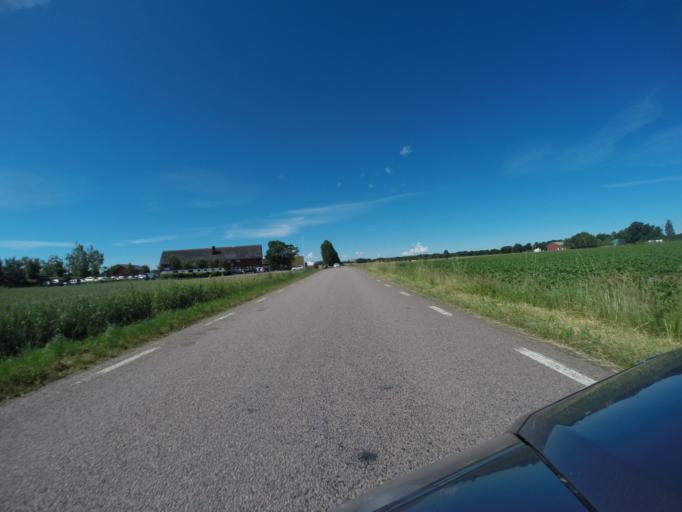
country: SE
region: Skane
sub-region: Helsingborg
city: Odakra
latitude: 56.1335
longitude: 12.7159
